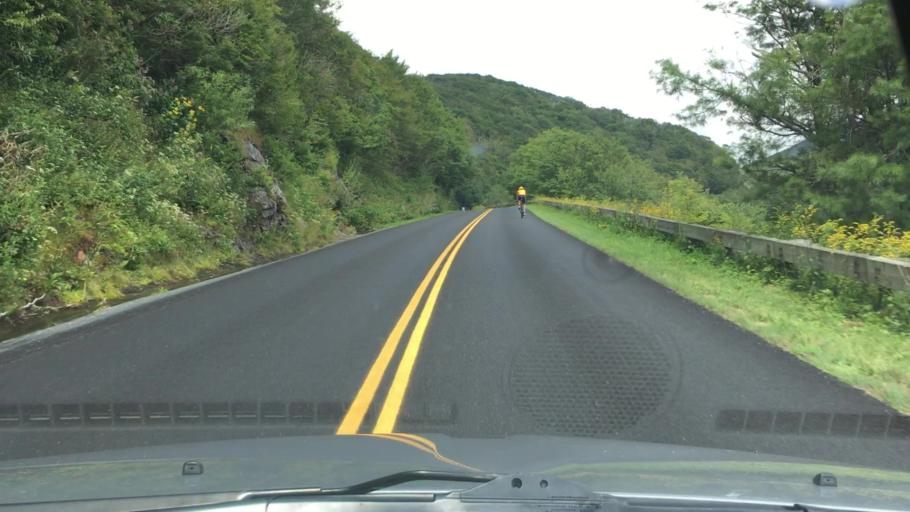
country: US
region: North Carolina
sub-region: Buncombe County
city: Swannanoa
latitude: 35.6925
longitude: -82.3833
